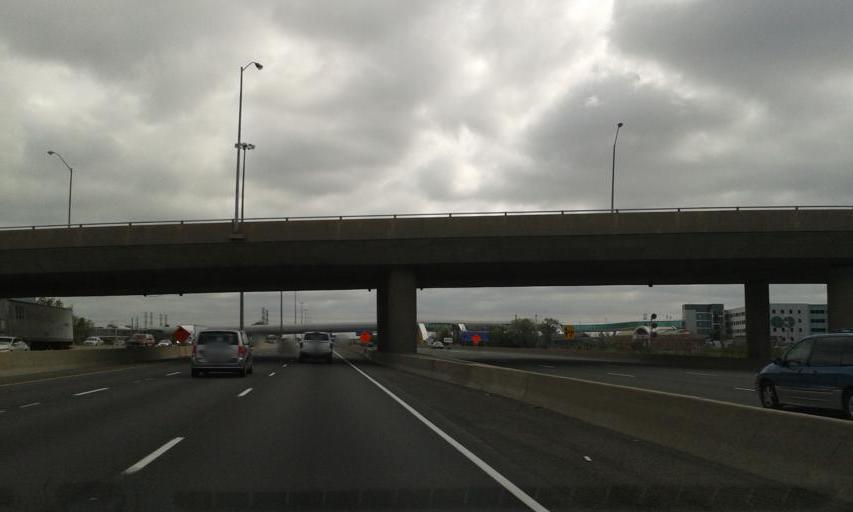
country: CA
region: Ontario
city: Ajax
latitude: 43.8299
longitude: -79.0896
